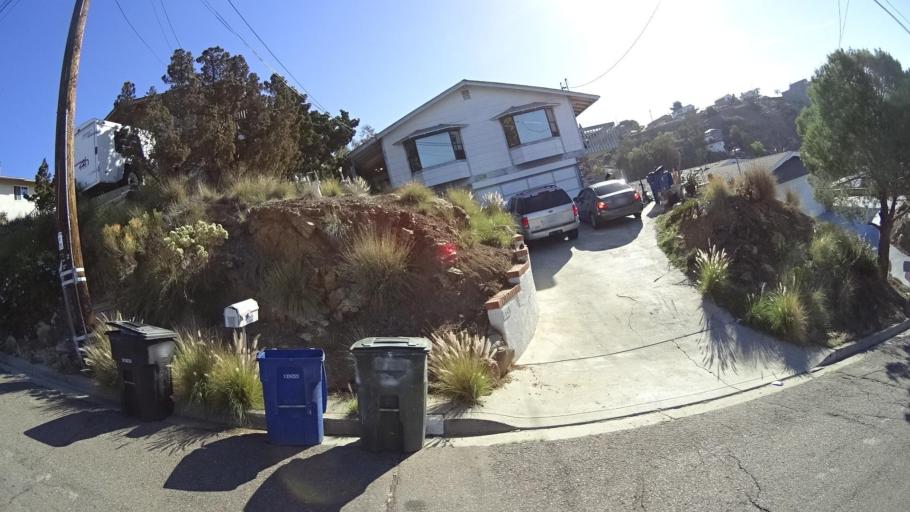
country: US
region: California
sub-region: San Diego County
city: La Presa
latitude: 32.7215
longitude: -116.9971
